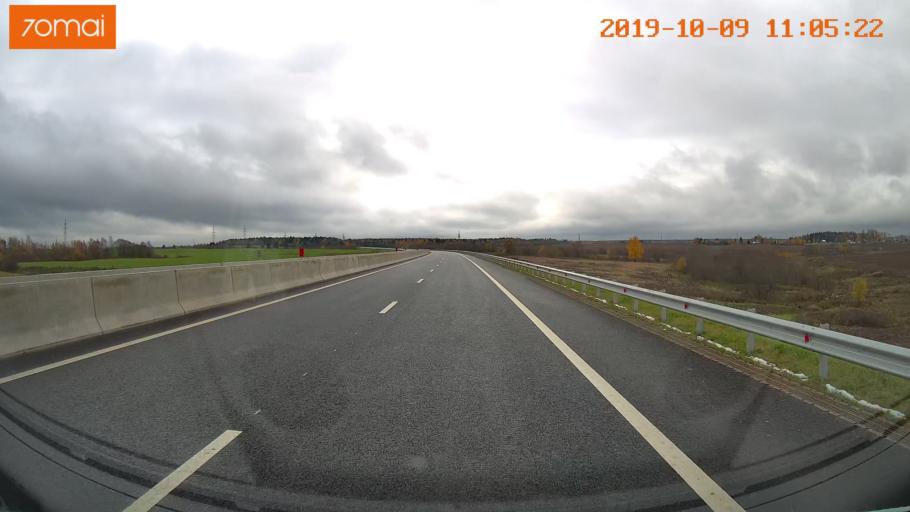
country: RU
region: Vologda
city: Molochnoye
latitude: 59.2011
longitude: 39.7592
